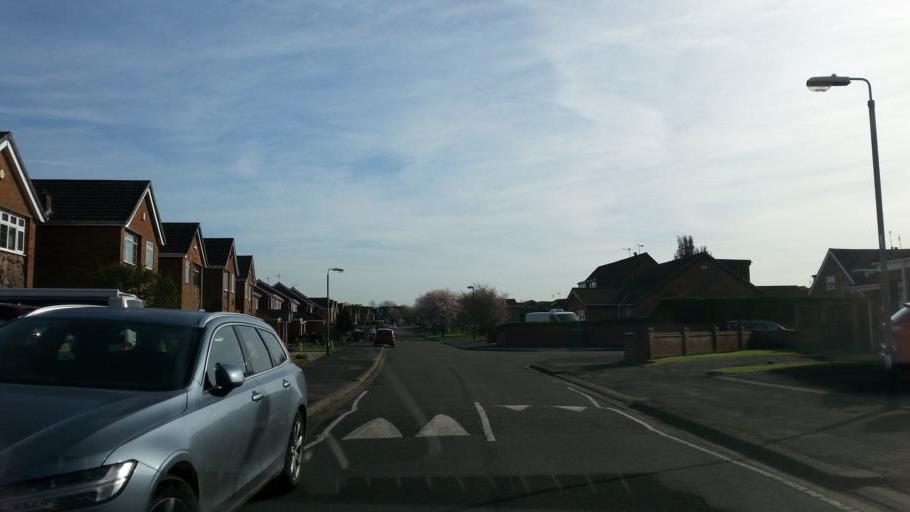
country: GB
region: England
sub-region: Warwickshire
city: Attleborough
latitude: 52.5012
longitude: -1.4314
